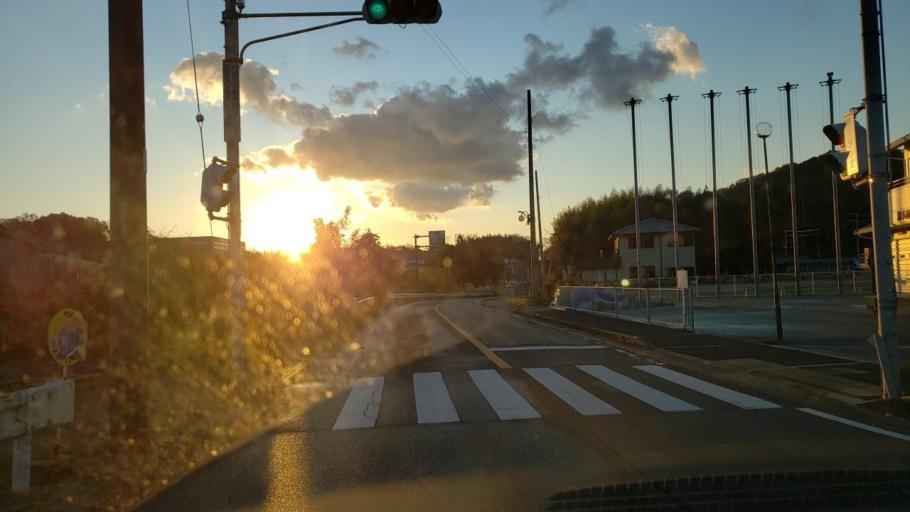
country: JP
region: Hyogo
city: Sumoto
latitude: 34.3992
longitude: 134.8183
